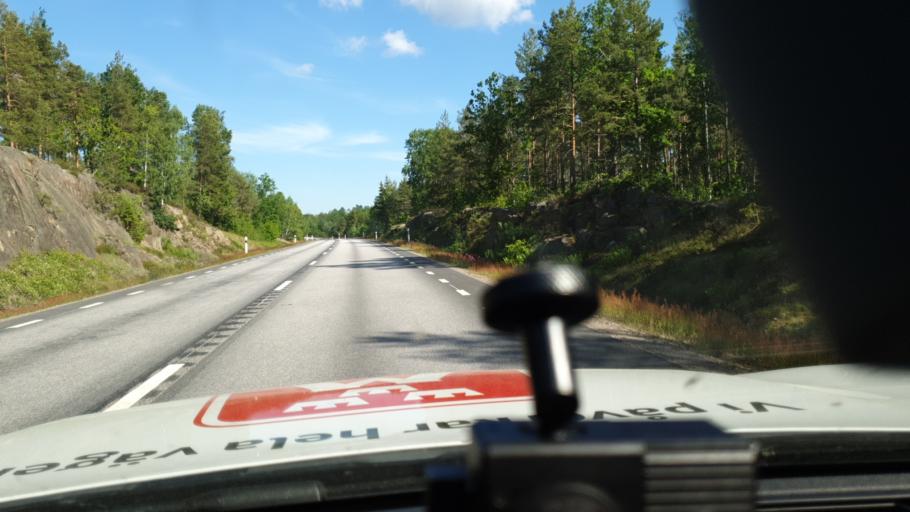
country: SE
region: Kalmar
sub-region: Vasterviks Kommun
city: Ankarsrum
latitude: 57.7119
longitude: 16.1165
